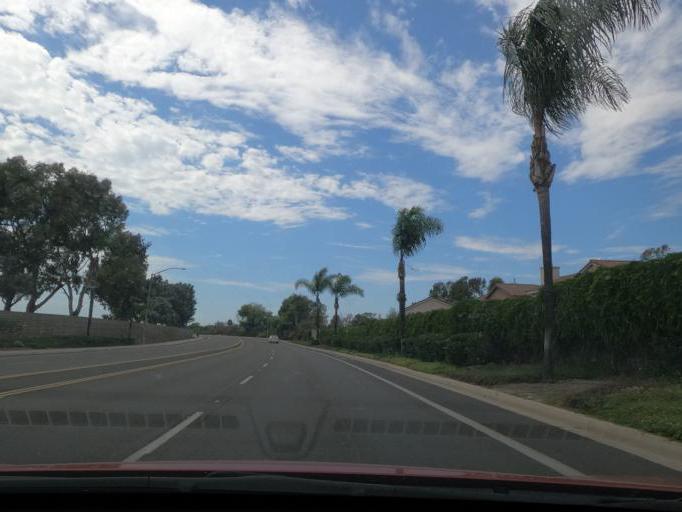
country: US
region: California
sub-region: San Diego County
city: Imperial Beach
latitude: 32.5506
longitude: -117.0554
